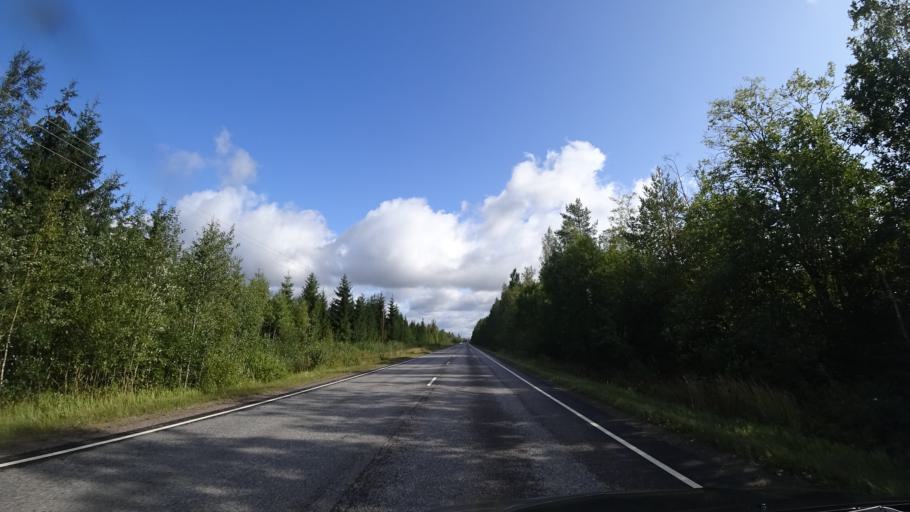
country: FI
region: Uusimaa
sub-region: Helsinki
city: Hyvinge
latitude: 60.5433
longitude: 24.9331
